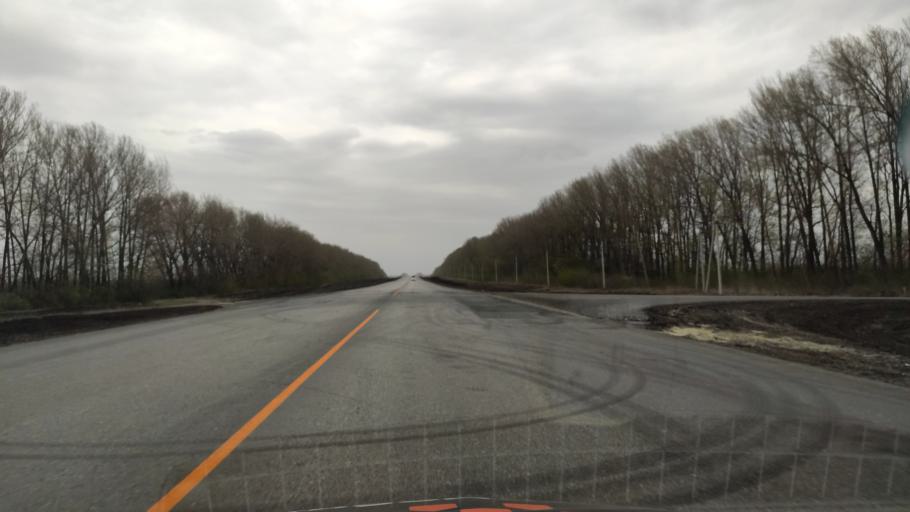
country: RU
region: Kursk
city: Gorshechnoye
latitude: 51.5475
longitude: 38.0737
